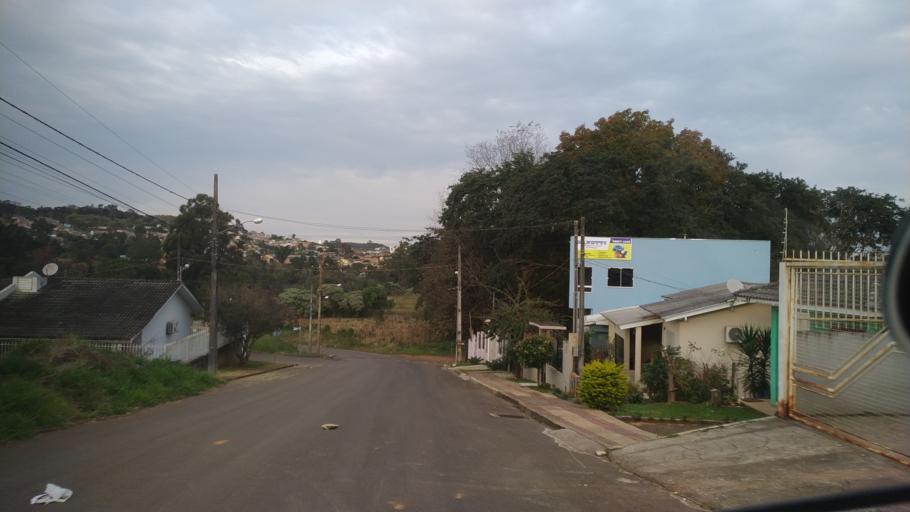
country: BR
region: Santa Catarina
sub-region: Chapeco
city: Chapeco
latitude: -27.1240
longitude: -52.5948
